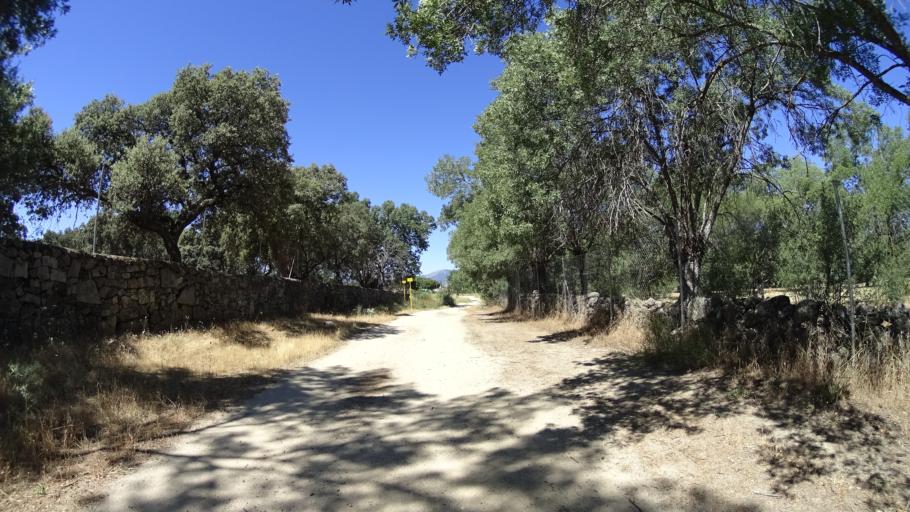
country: ES
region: Madrid
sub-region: Provincia de Madrid
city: Alpedrete
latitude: 40.6458
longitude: -4.0191
